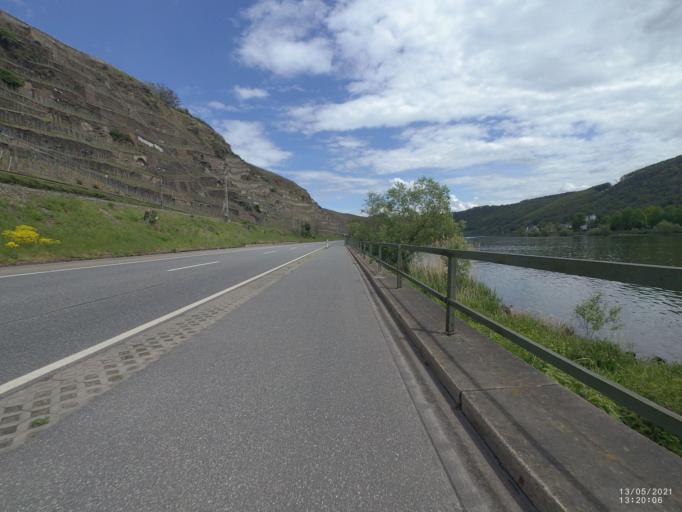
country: DE
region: Rheinland-Pfalz
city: Winningen
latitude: 50.3227
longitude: 7.5330
